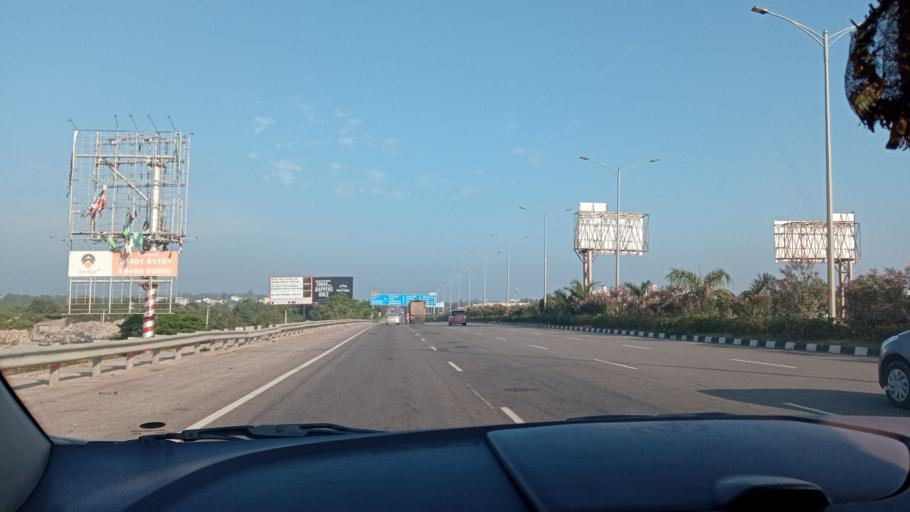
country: IN
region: Telangana
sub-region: Hyderabad
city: Hyderabad
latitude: 17.3291
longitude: 78.3722
